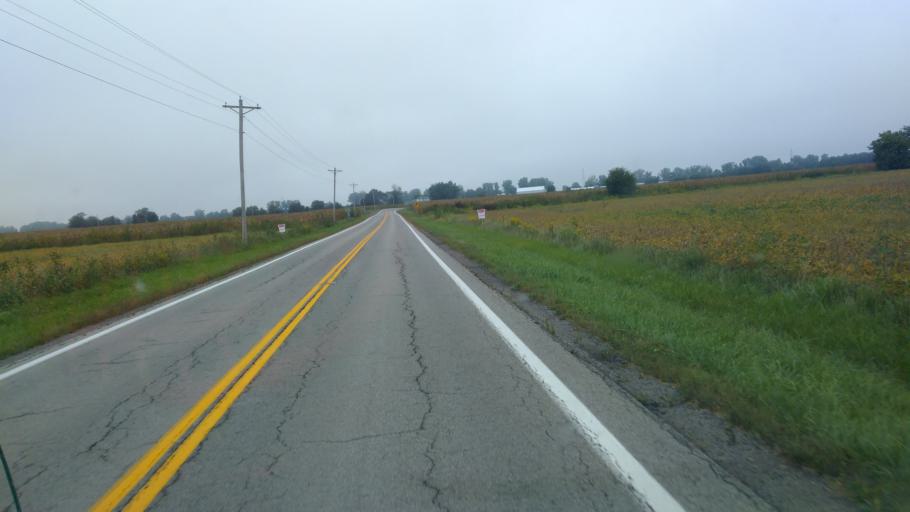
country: US
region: Ohio
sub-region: Logan County
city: Northwood
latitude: 40.4752
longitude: -83.5785
